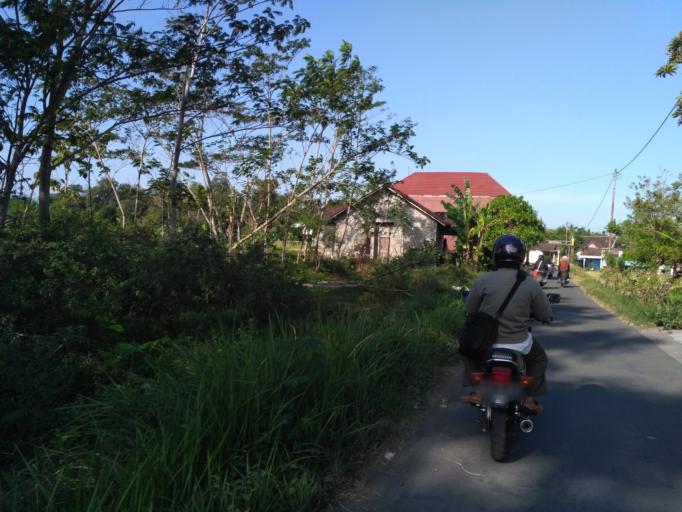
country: ID
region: Daerah Istimewa Yogyakarta
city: Depok
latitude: -7.7741
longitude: 110.4262
